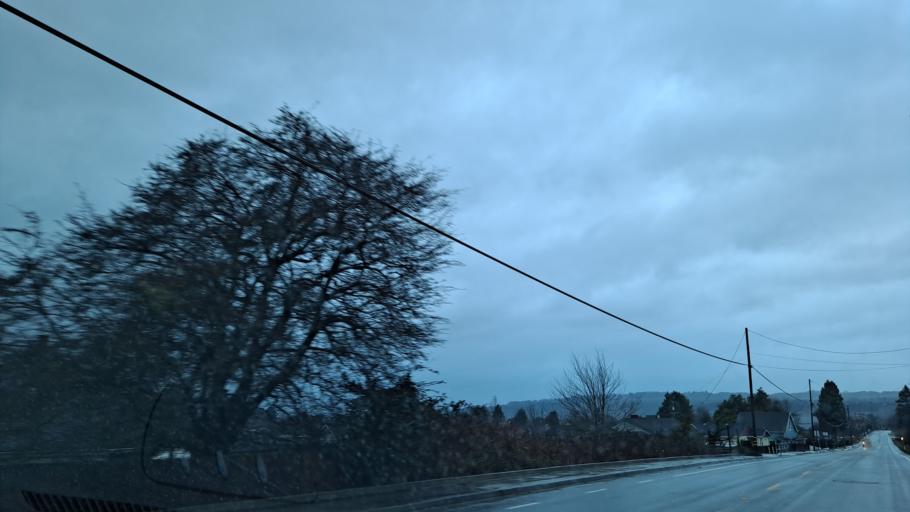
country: US
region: California
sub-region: Humboldt County
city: Fortuna
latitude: 40.5727
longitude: -124.1275
